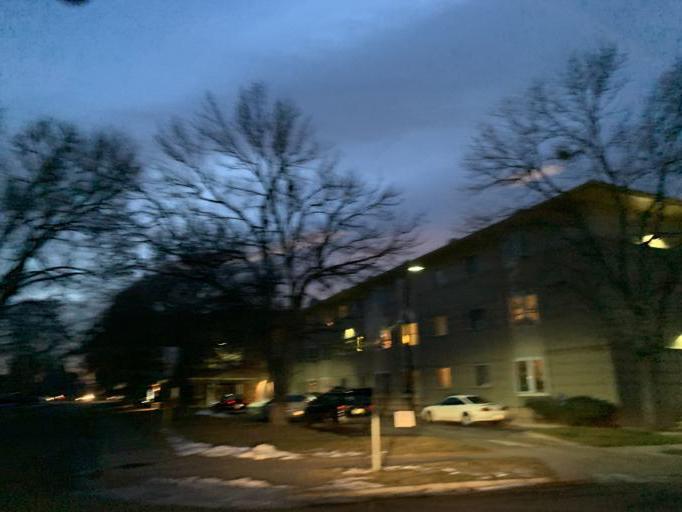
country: US
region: Colorado
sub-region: Jefferson County
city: Edgewater
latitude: 39.7710
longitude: -105.0405
